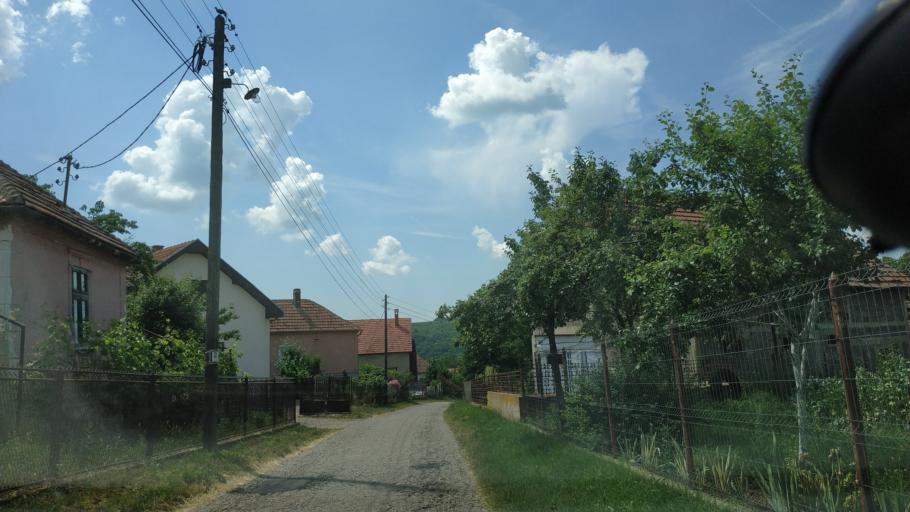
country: RS
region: Central Serbia
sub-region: Nisavski Okrug
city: Aleksinac
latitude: 43.5993
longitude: 21.6914
